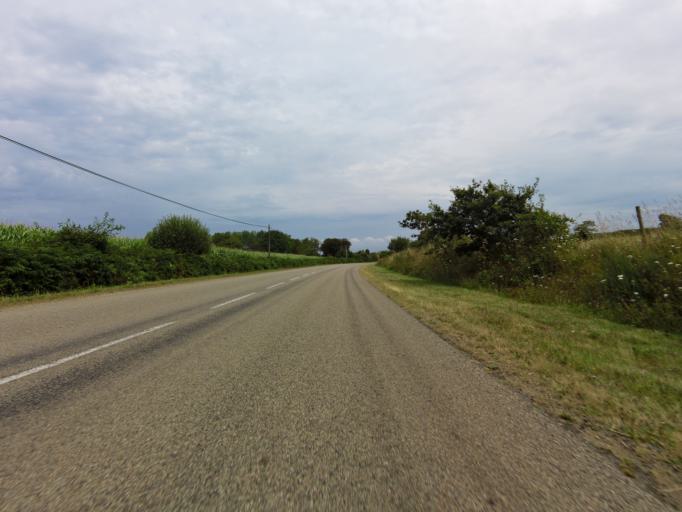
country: FR
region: Brittany
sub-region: Departement du Finistere
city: Poullan-sur-Mer
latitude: 48.0813
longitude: -4.4274
